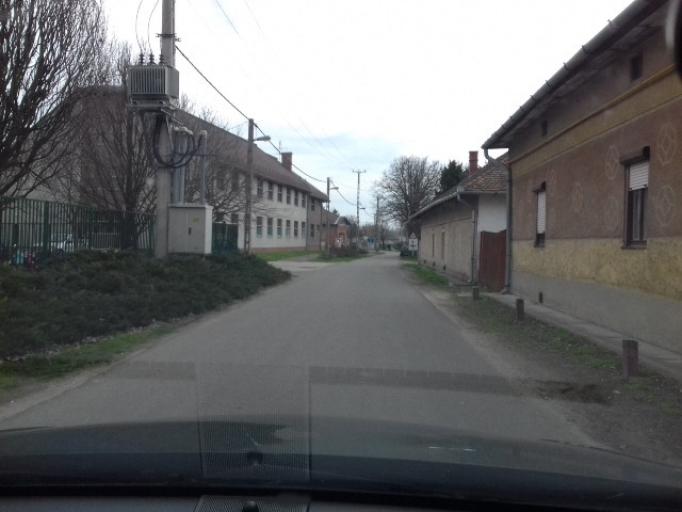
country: HU
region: Bacs-Kiskun
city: Tiszakecske
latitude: 46.8864
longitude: 20.1185
